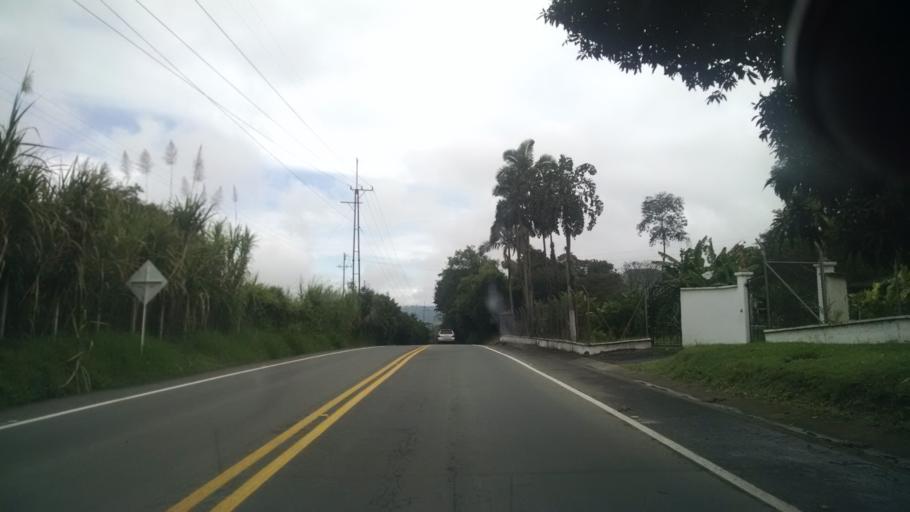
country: CO
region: Caldas
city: Palestina
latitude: 5.0215
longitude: -75.5971
